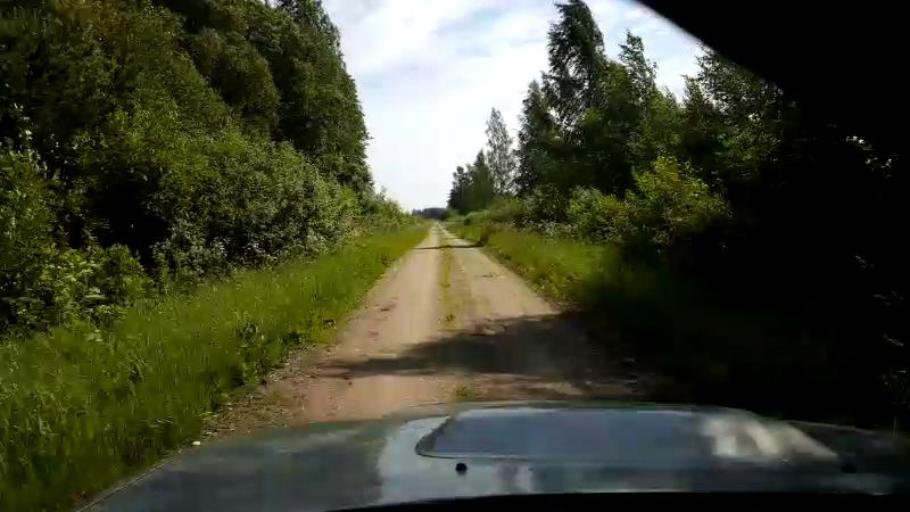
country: EE
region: Paernumaa
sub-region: Sindi linn
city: Sindi
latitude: 58.5196
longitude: 24.6696
